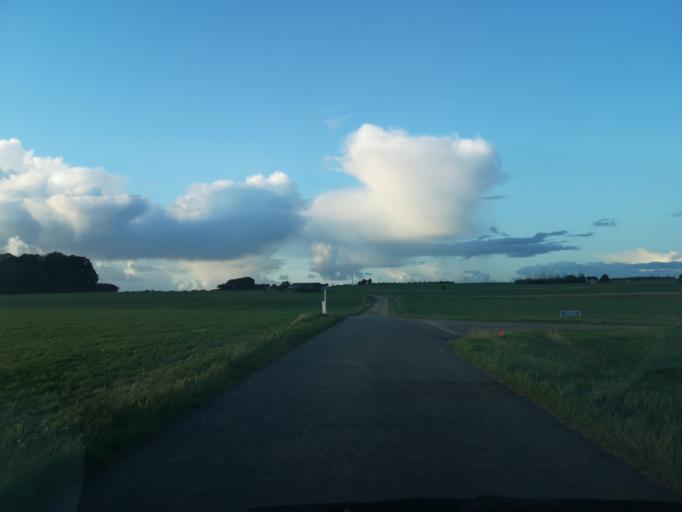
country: DK
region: Central Jutland
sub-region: Ringkobing-Skjern Kommune
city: Videbaek
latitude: 56.0444
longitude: 8.5820
